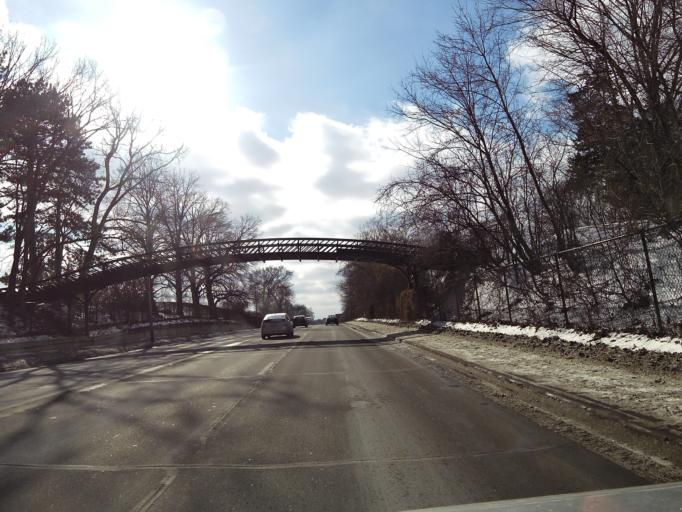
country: US
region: Minnesota
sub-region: Hennepin County
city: Saint Louis Park
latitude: 44.9442
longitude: -93.3246
